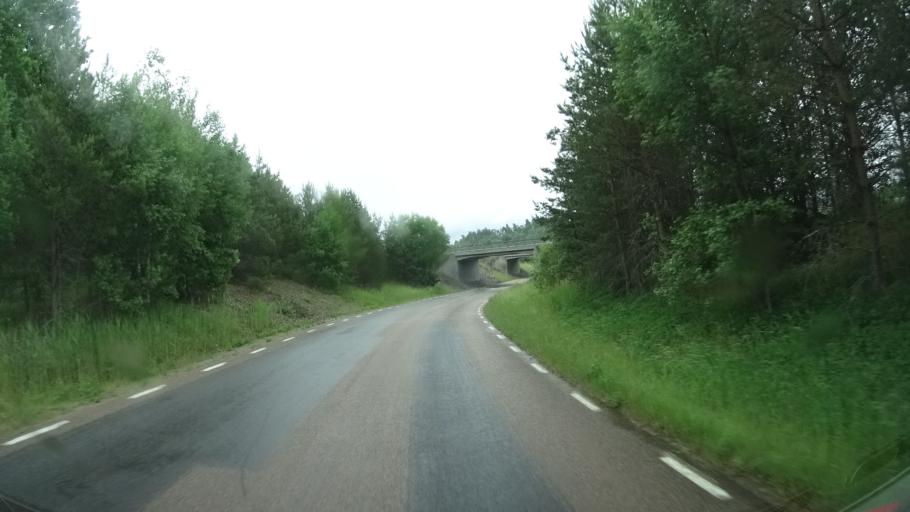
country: SE
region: Soedermanland
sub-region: Nykopings Kommun
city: Stigtomta
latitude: 58.7593
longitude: 16.7097
